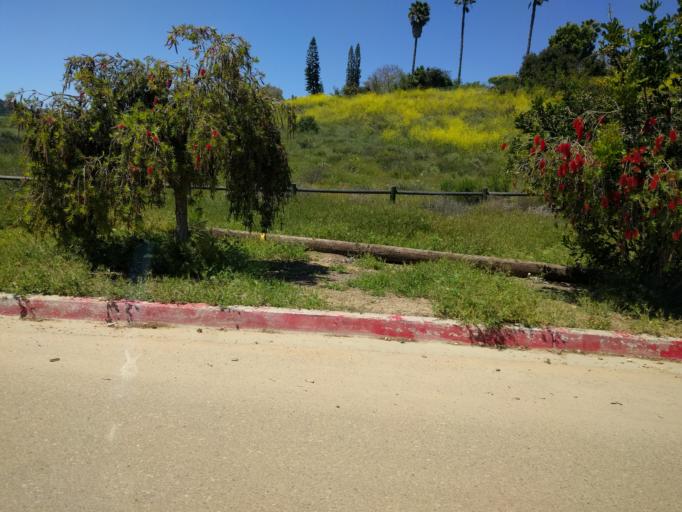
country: US
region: California
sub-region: San Diego County
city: Fairbanks Ranch
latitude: 32.9417
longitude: -117.1357
